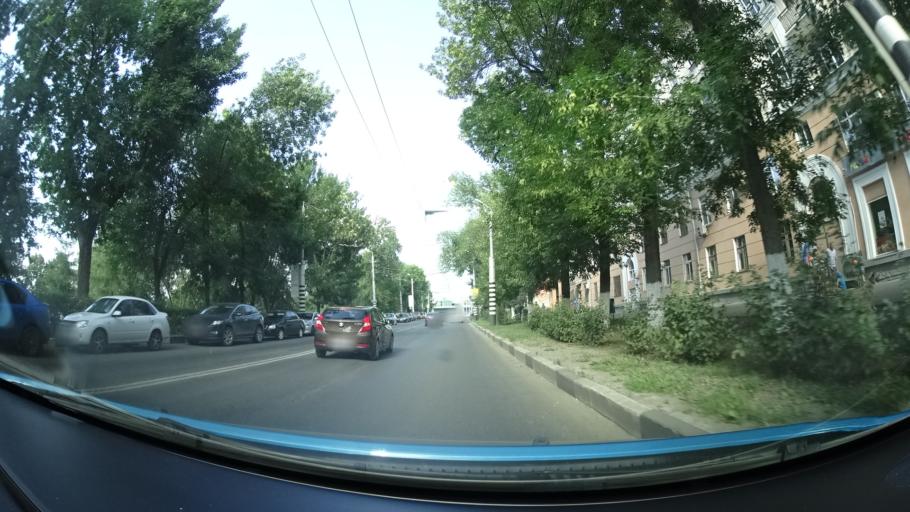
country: RU
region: Samara
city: Samara
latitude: 53.2101
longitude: 50.1204
